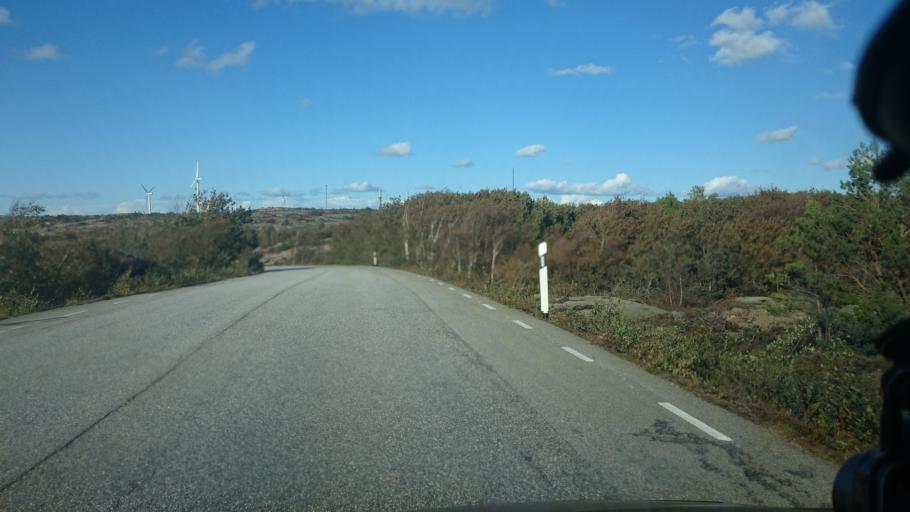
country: SE
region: Vaestra Goetaland
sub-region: Lysekils Kommun
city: Lysekil
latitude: 58.3238
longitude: 11.4162
